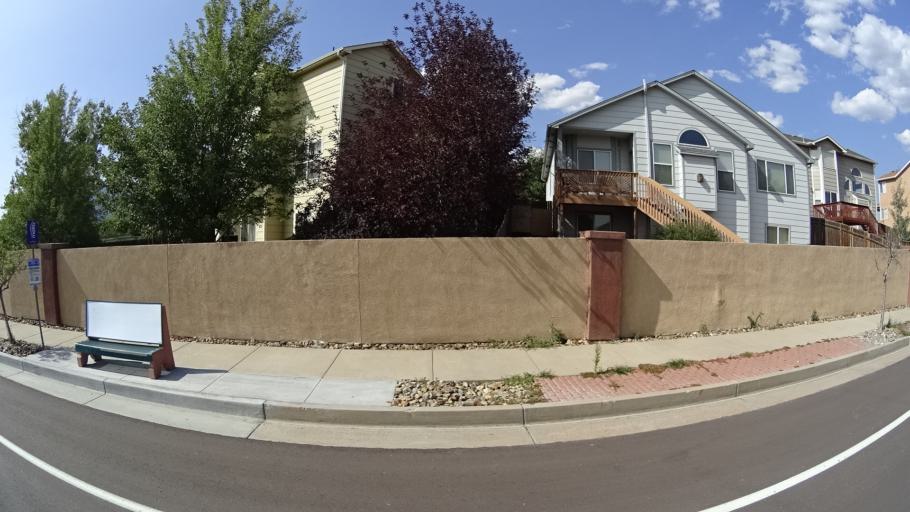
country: US
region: Colorado
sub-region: El Paso County
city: Colorado Springs
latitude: 38.8255
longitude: -104.8511
